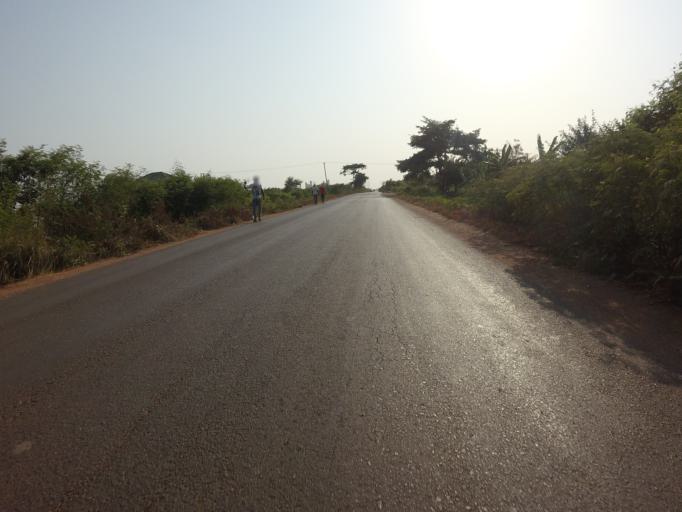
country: GH
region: Greater Accra
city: Tema
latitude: 5.6900
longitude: 0.0472
